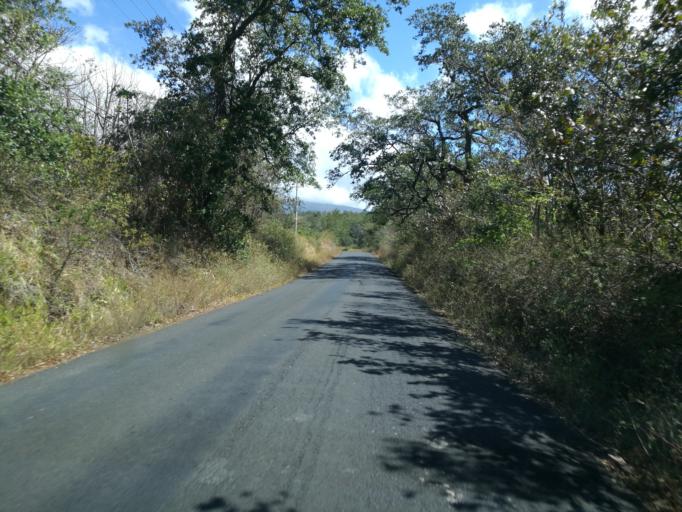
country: CR
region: Guanacaste
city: Liberia
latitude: 10.7442
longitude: -85.3834
